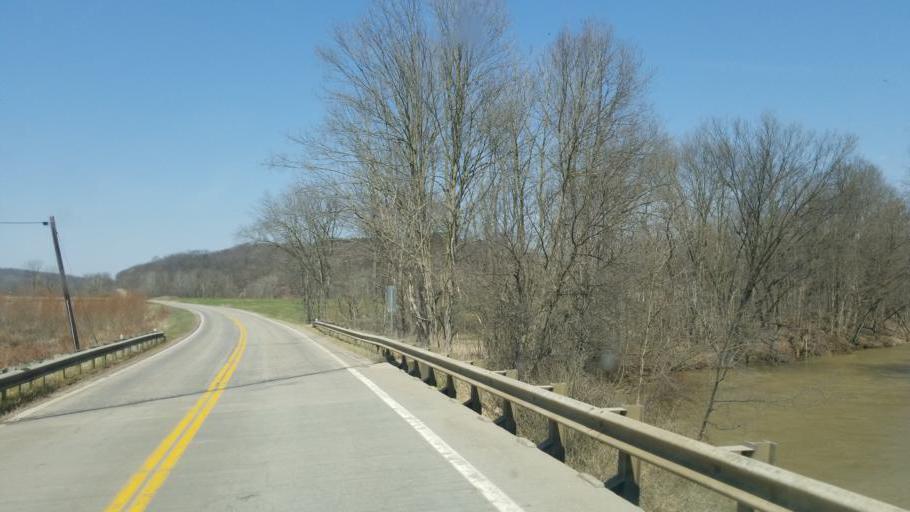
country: US
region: Ohio
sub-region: Ashland County
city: Loudonville
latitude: 40.7092
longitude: -82.1614
